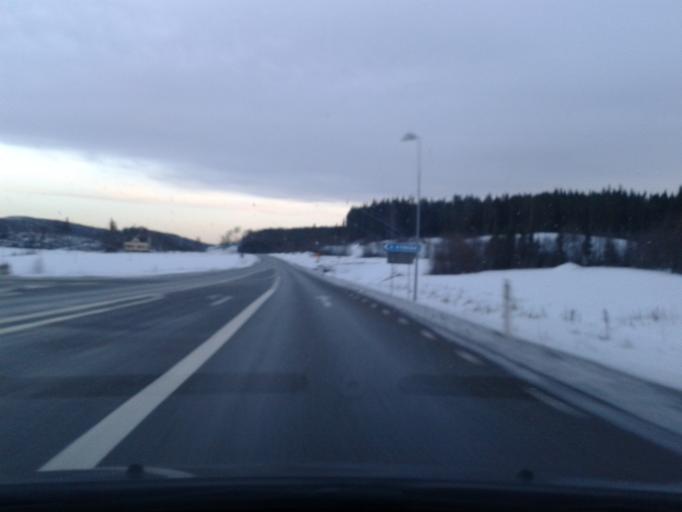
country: SE
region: Vaesternorrland
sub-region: Kramfors Kommun
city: Bollstabruk
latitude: 63.0394
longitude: 17.6482
